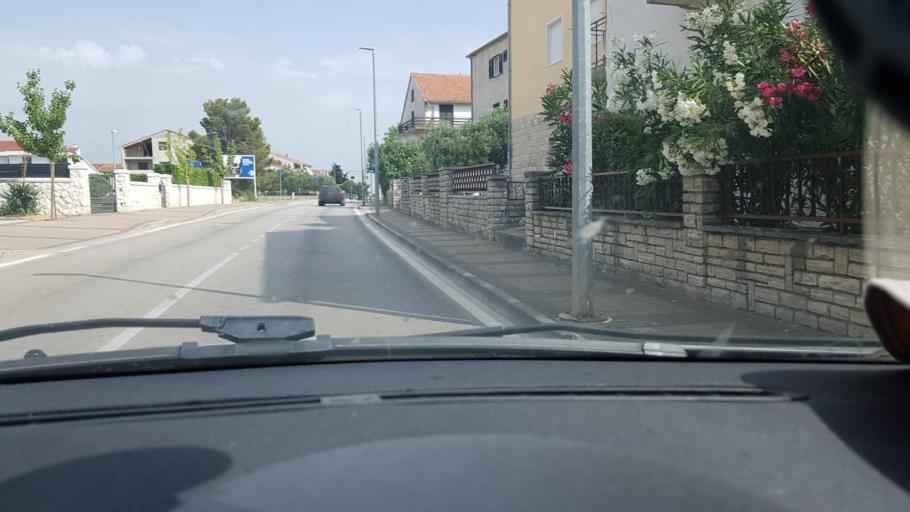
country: HR
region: Sibensko-Kniniska
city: Vodice
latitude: 43.7604
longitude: 15.7865
